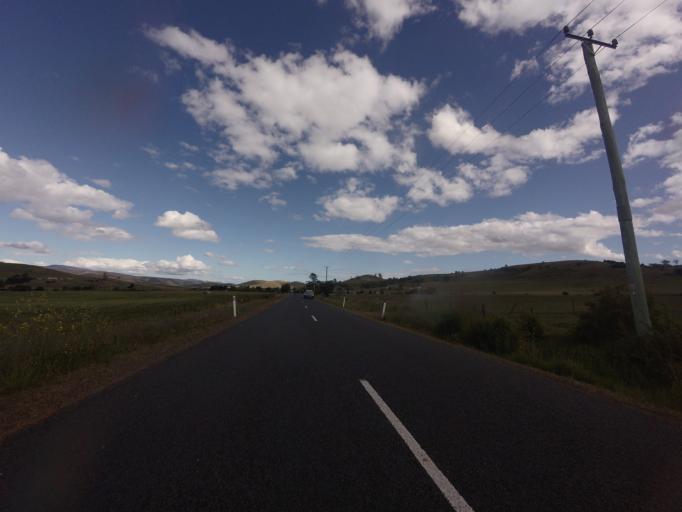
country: AU
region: Tasmania
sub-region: Brighton
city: Bridgewater
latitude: -42.5271
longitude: 147.3591
